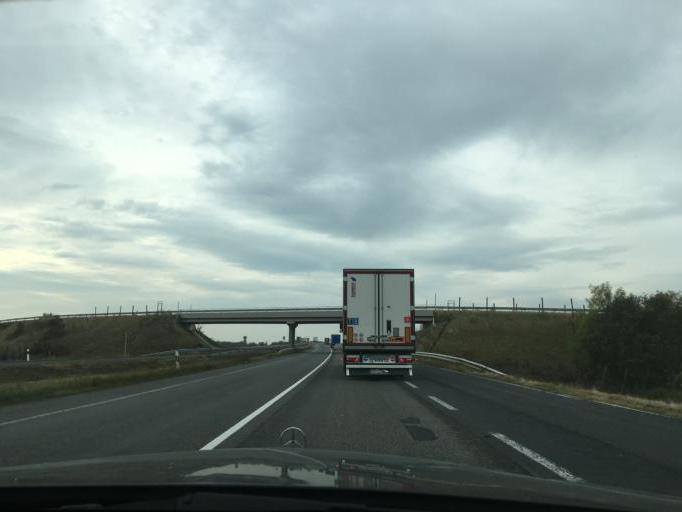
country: HU
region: Gyor-Moson-Sopron
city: Rajka
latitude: 47.9416
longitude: 17.1662
